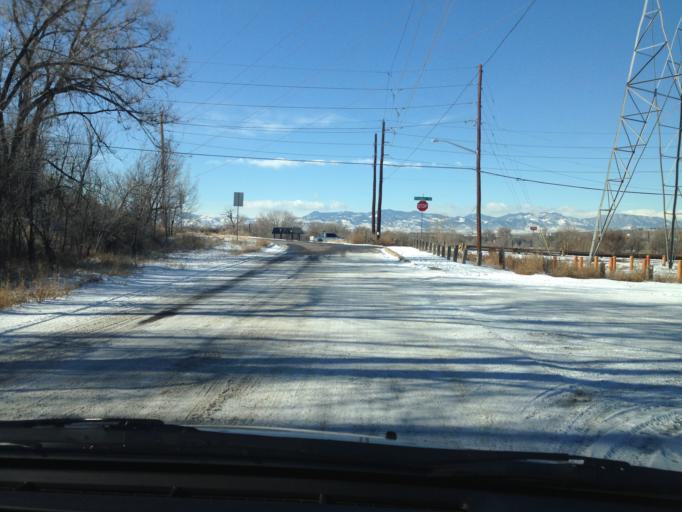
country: US
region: Colorado
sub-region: Adams County
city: Berkley
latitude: 39.7971
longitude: -105.0340
